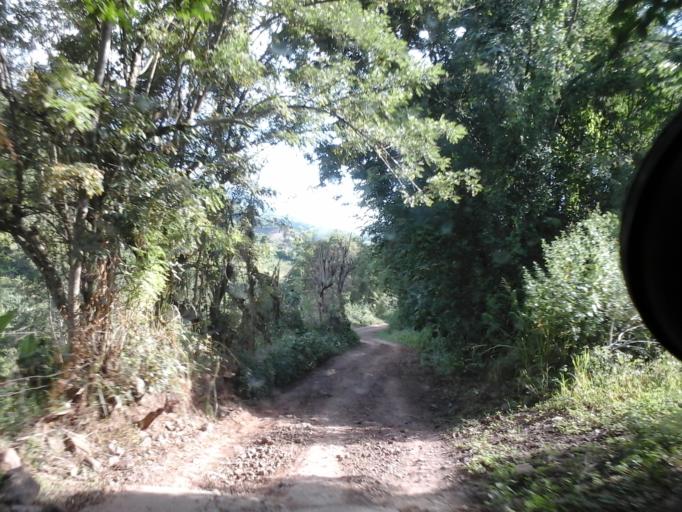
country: CO
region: Cesar
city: San Diego
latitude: 10.2660
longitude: -73.1019
